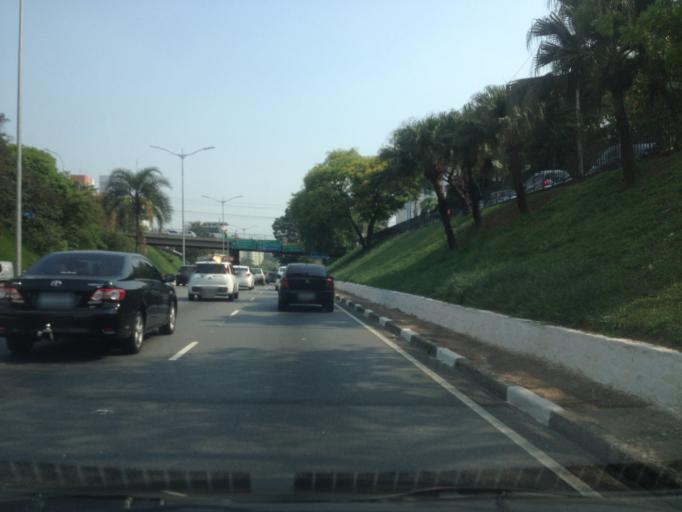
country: BR
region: Sao Paulo
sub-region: Sao Paulo
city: Sao Paulo
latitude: -23.5953
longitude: -46.6508
